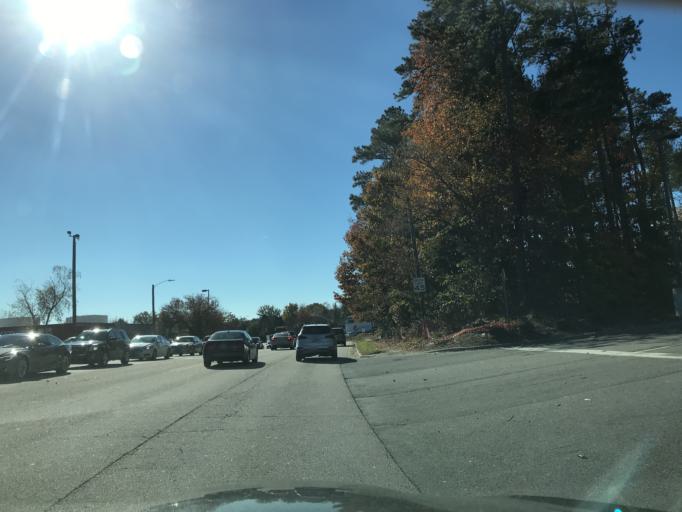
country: US
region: North Carolina
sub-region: Wake County
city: Raleigh
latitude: 35.8626
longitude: -78.5990
